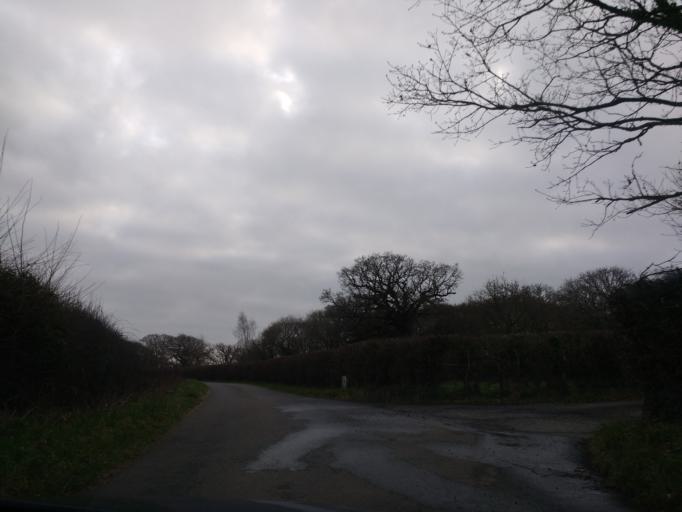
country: GB
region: England
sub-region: Isle of Wight
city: Shalfleet
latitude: 50.6954
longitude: -1.3949
